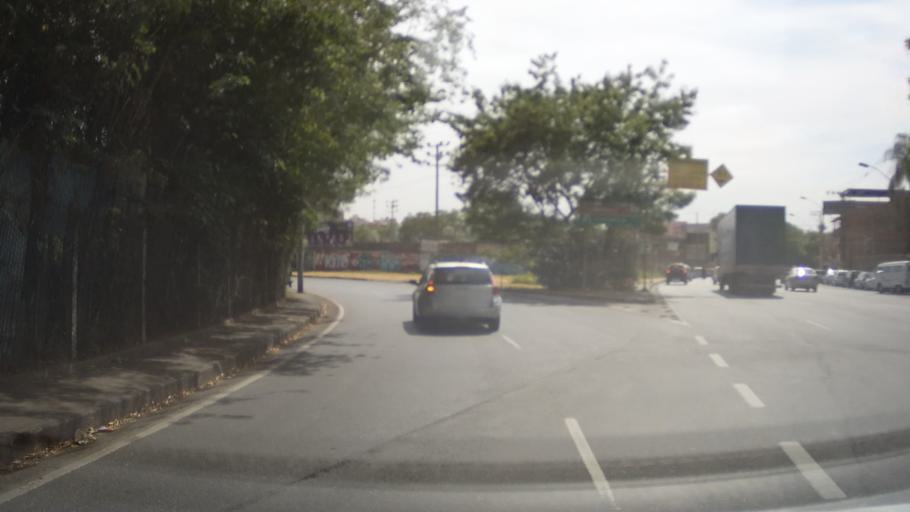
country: BR
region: Minas Gerais
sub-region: Belo Horizonte
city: Belo Horizonte
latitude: -19.9242
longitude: -43.9833
